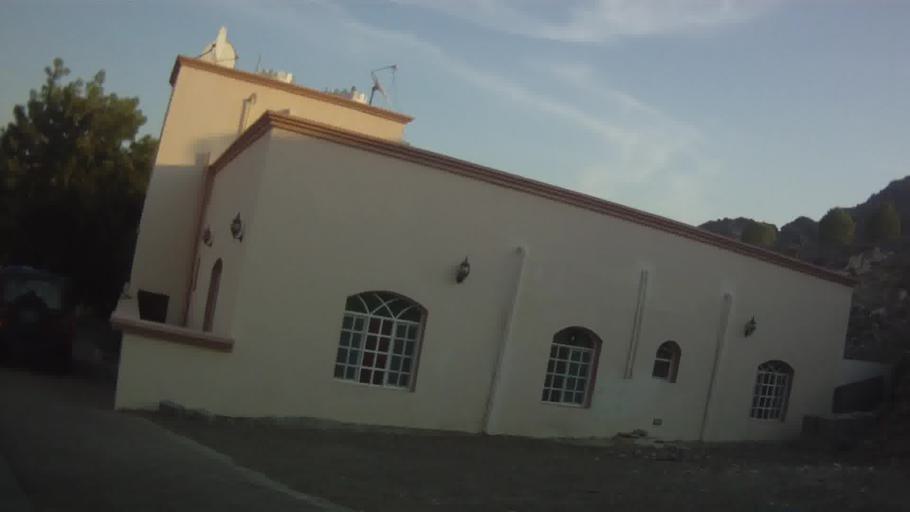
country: OM
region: Muhafazat Masqat
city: Muscat
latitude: 23.6177
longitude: 58.5875
